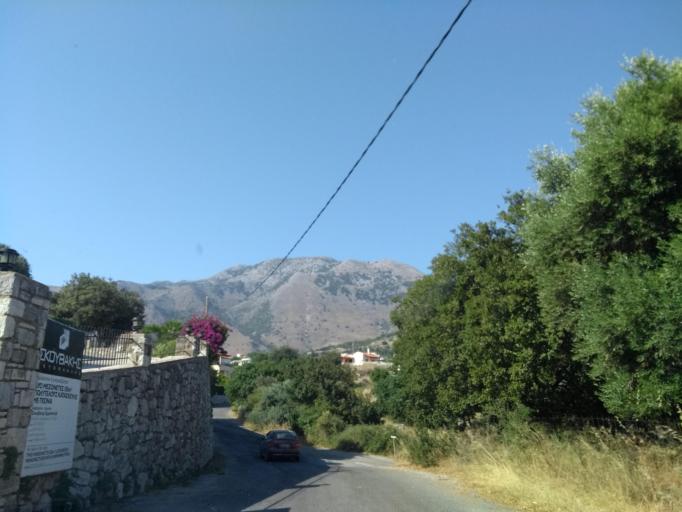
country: GR
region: Crete
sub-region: Nomos Chanias
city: Georgioupolis
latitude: 35.3209
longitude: 24.2983
